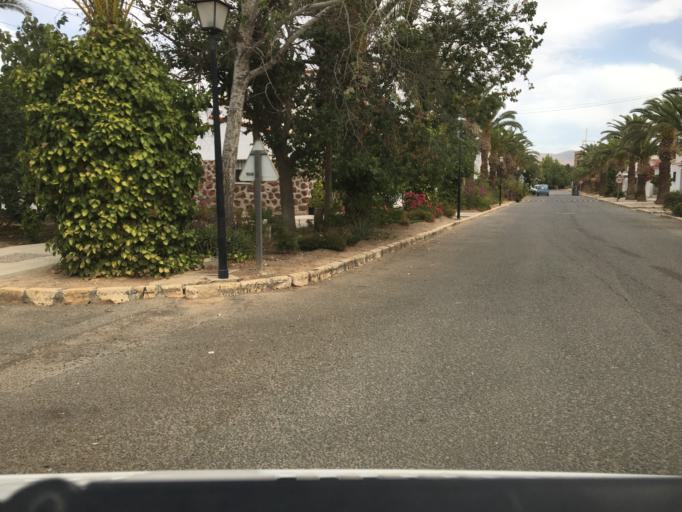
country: ES
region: Andalusia
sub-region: Provincia de Almeria
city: Huercal-Overa
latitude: 37.4202
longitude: -1.8777
